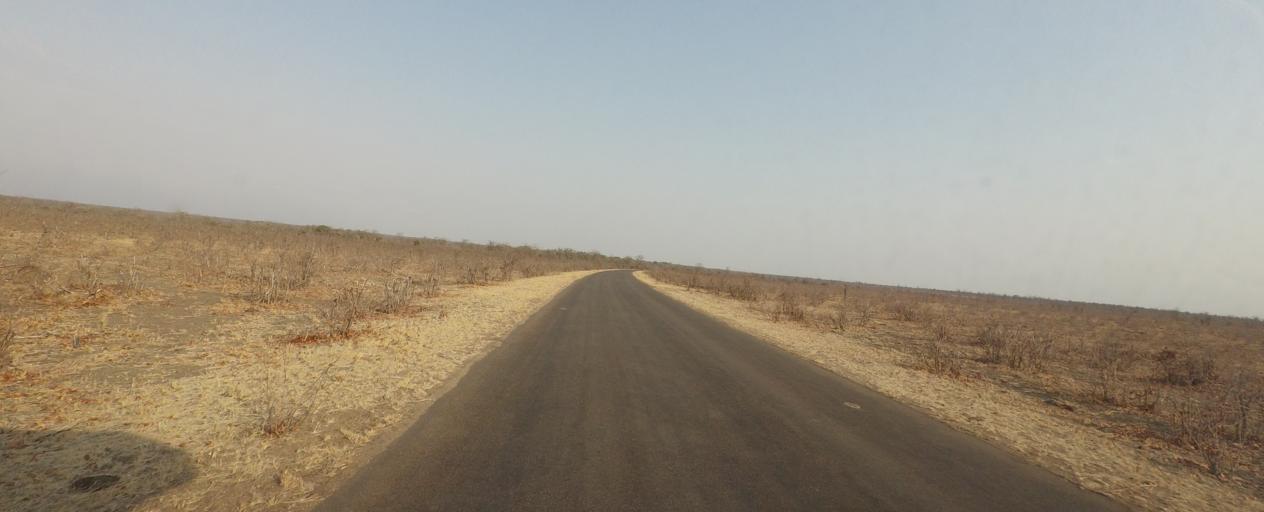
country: ZA
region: Limpopo
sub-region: Mopani District Municipality
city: Giyani
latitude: -23.0756
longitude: 31.4101
